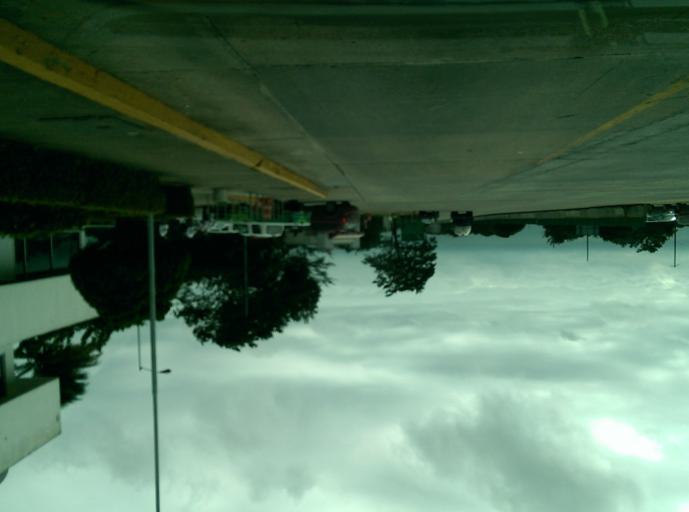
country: MX
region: Veracruz
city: Villa Nanchital
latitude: 18.0136
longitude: -94.3969
